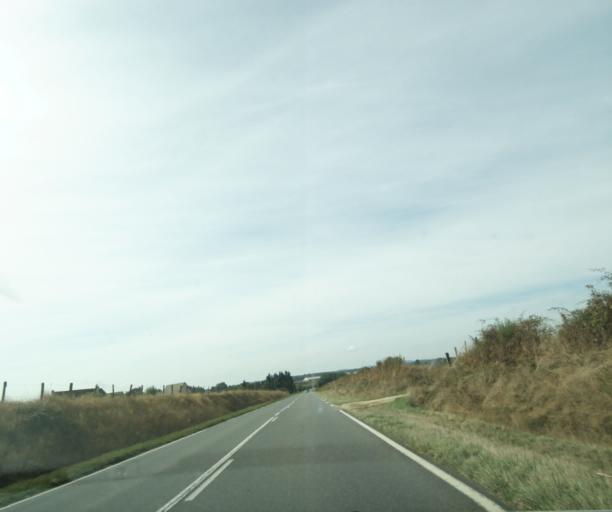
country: FR
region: Auvergne
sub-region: Departement de l'Allier
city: Saint-Francois
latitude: 46.3725
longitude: 3.8626
